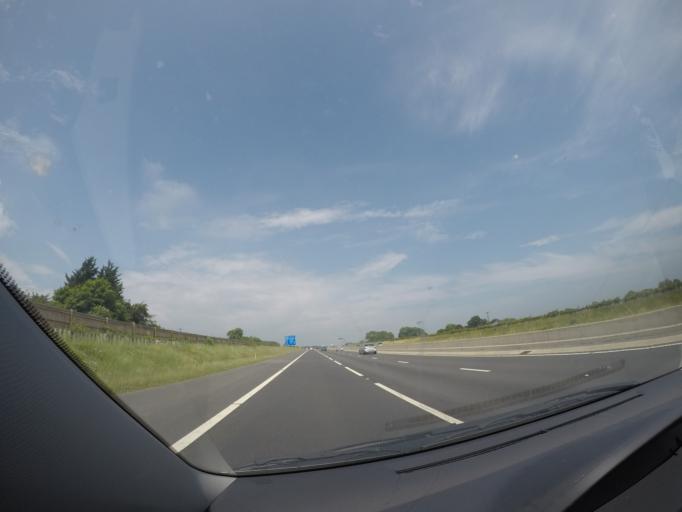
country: GB
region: England
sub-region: North Yorkshire
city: Catterick
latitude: 54.4286
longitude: -1.6666
